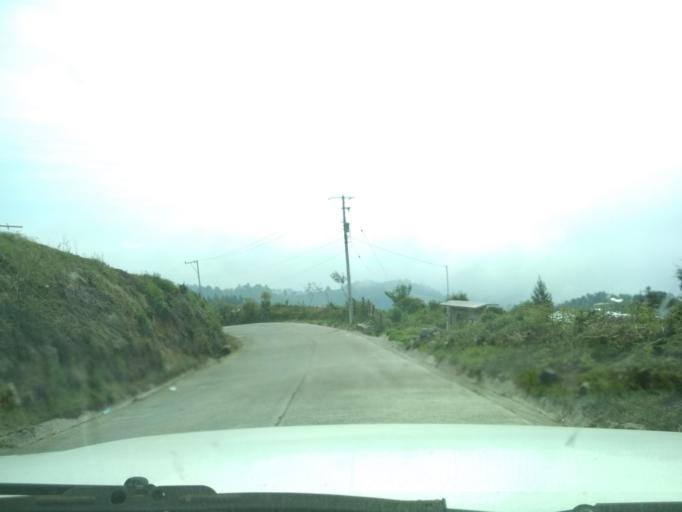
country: MX
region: Veracruz
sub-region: Mariano Escobedo
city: San Isidro el Berro
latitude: 18.9752
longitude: -97.2079
